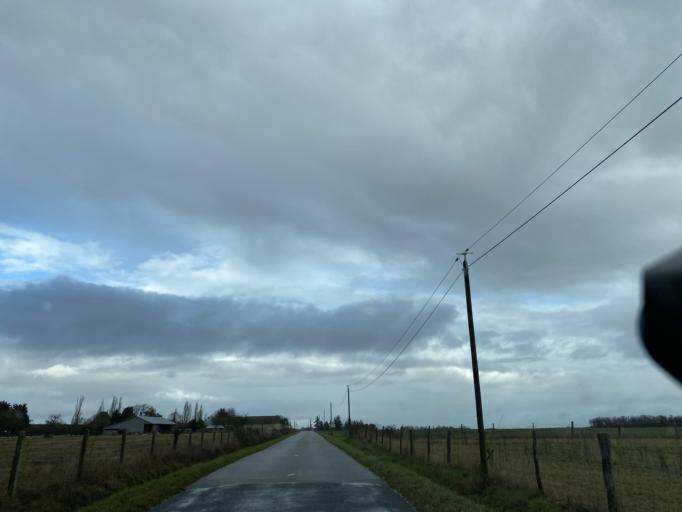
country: FR
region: Haute-Normandie
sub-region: Departement de l'Eure
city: Tillieres-sur-Avre
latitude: 48.7831
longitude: 1.0598
